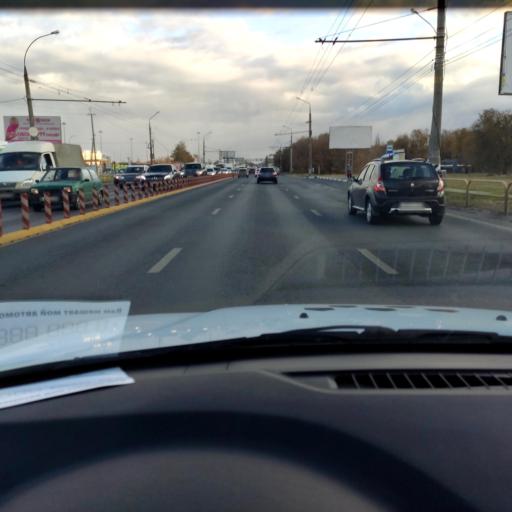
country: RU
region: Samara
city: Tol'yatti
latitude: 53.5433
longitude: 49.3832
